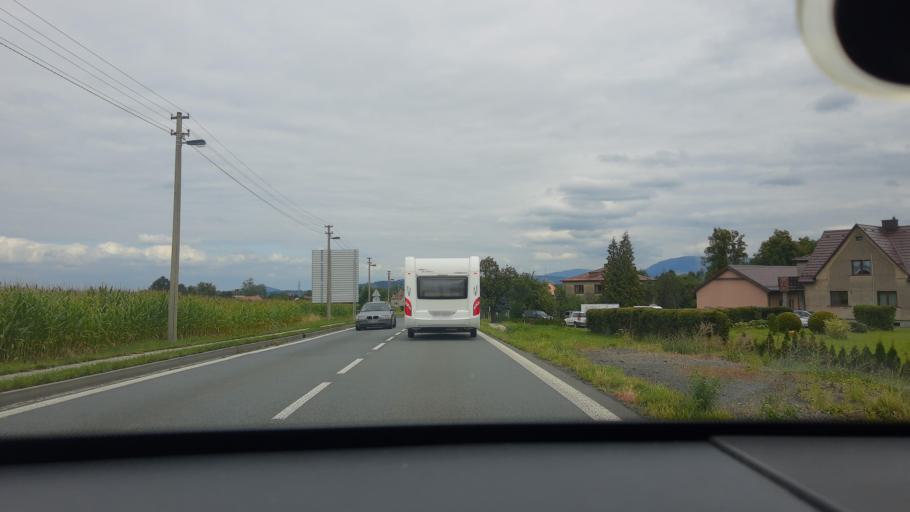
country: CZ
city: Ropice
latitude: 49.6777
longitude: 18.6061
